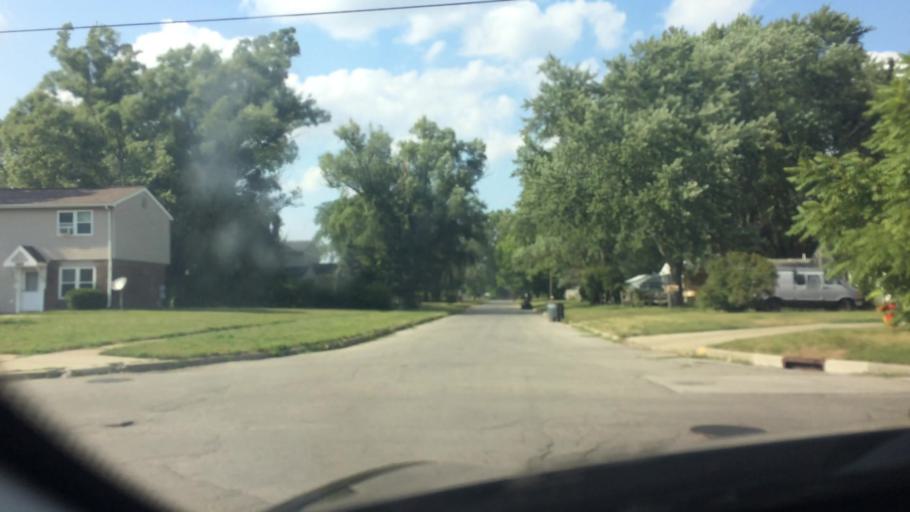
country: US
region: Ohio
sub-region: Lucas County
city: Ottawa Hills
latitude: 41.6272
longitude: -83.6209
